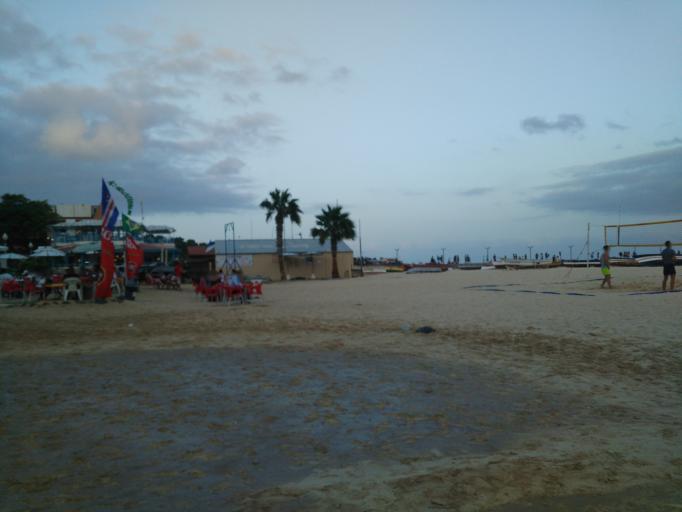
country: CV
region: Sal
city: Santa Maria
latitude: 16.5976
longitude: -22.9086
